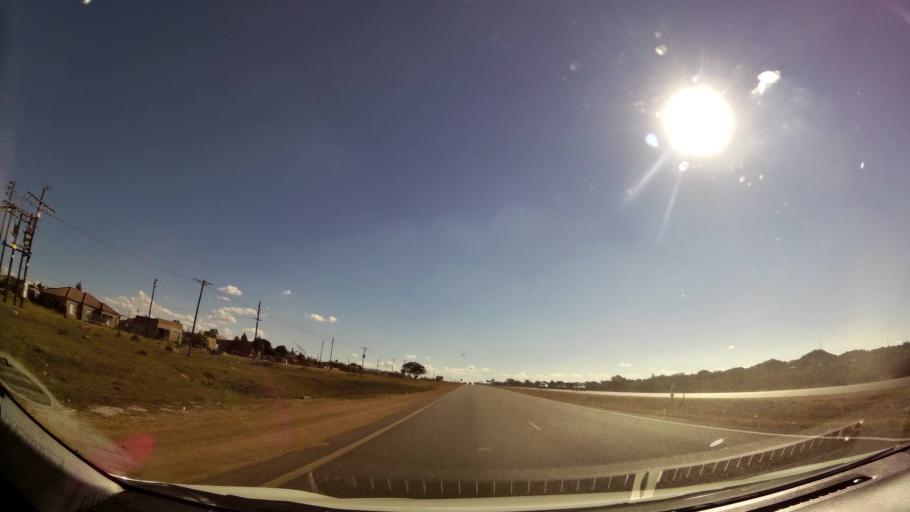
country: ZA
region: Limpopo
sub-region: Capricorn District Municipality
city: Mankoeng
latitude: -23.9010
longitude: 29.7431
